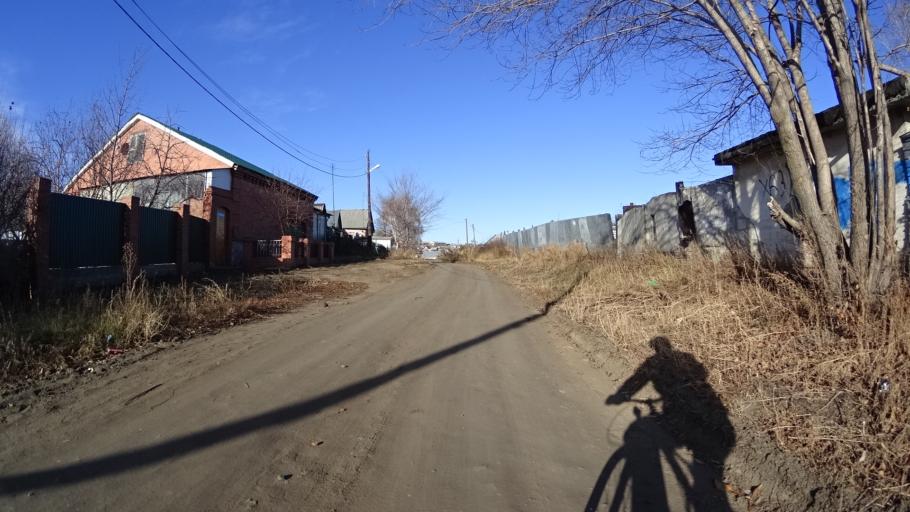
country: RU
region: Chelyabinsk
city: Troitsk
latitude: 54.0918
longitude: 61.5867
